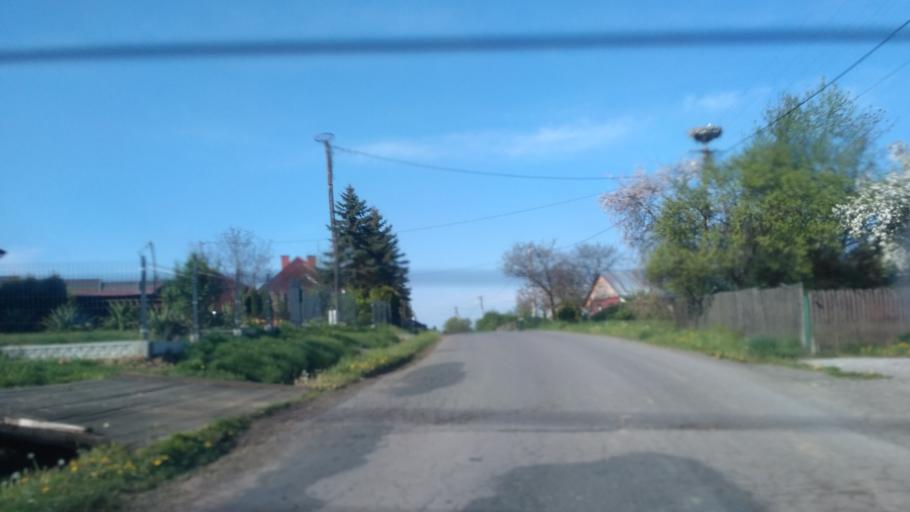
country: PL
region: Subcarpathian Voivodeship
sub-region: Powiat jaroslawski
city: Kramarzowka
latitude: 49.8463
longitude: 22.5144
